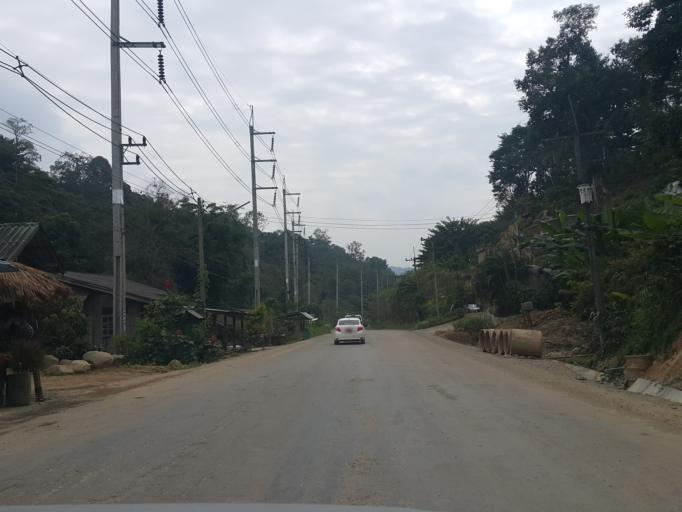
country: TH
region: Chiang Mai
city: Mae Taeng
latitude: 19.1698
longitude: 98.6913
